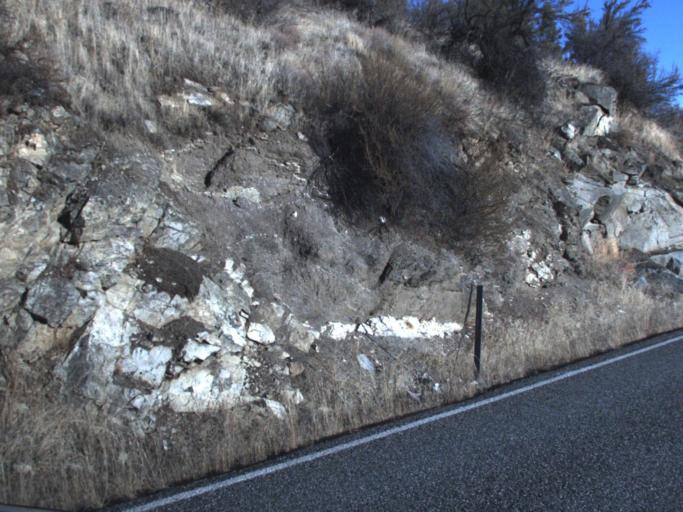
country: US
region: Washington
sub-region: Okanogan County
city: Coulee Dam
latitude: 48.0163
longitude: -118.6764
